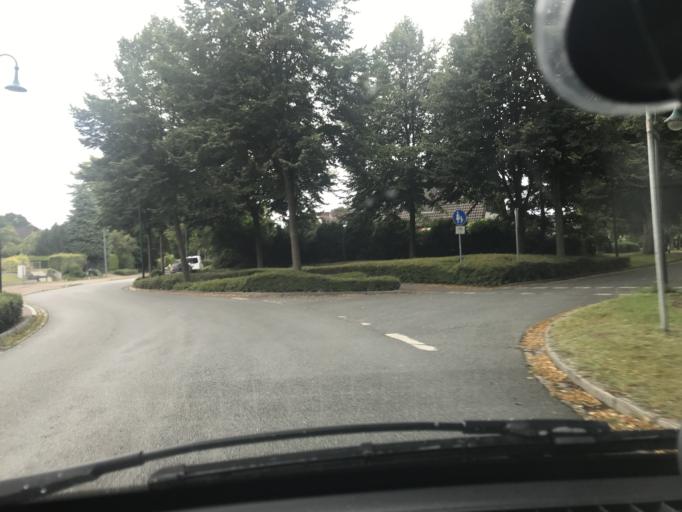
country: DE
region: Schleswig-Holstein
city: Grosshansdorf
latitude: 53.6511
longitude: 10.2674
